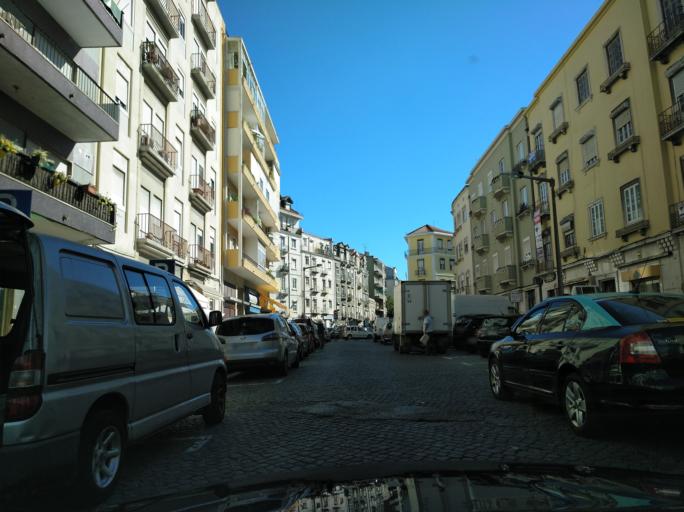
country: PT
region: Lisbon
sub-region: Lisbon
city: Lisbon
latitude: 38.7343
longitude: -9.1318
